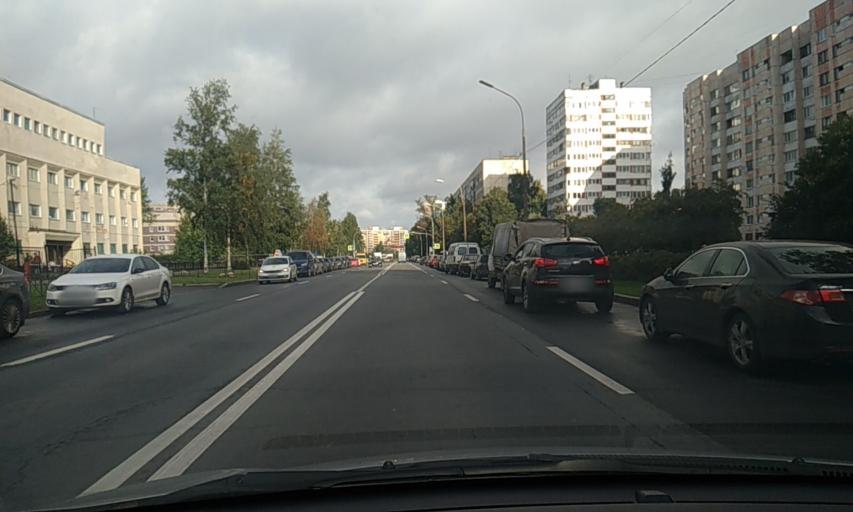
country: RU
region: St.-Petersburg
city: Dachnoye
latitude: 59.8358
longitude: 30.2166
